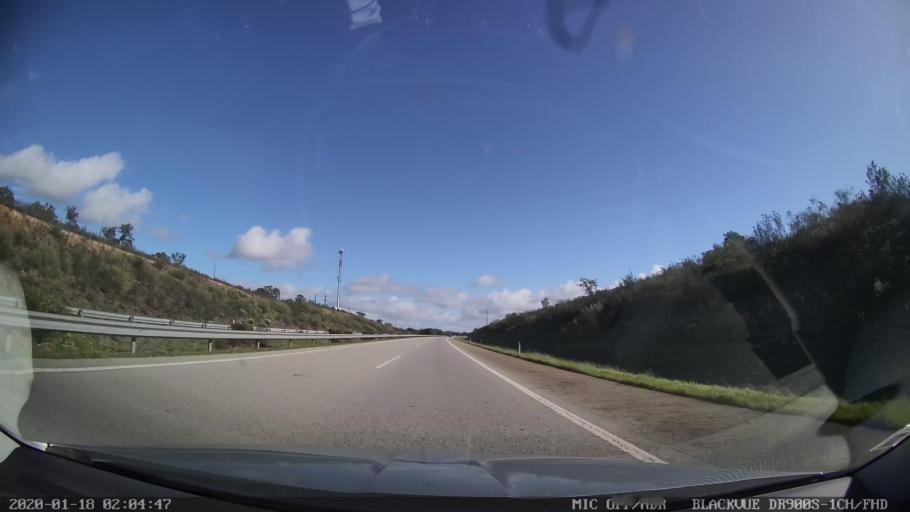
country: PT
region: Evora
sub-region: Vendas Novas
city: Vendas Novas
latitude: 38.6488
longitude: -8.4120
